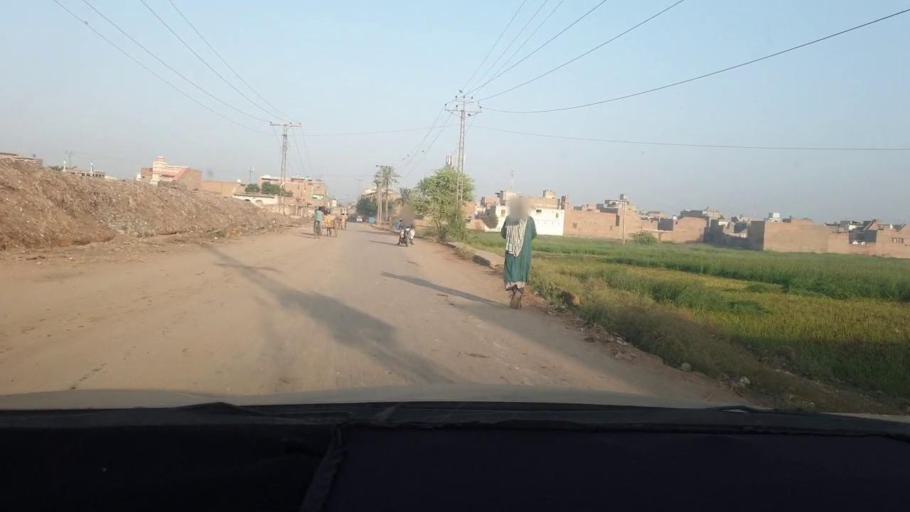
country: PK
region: Sindh
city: Larkana
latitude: 27.5416
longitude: 68.2165
